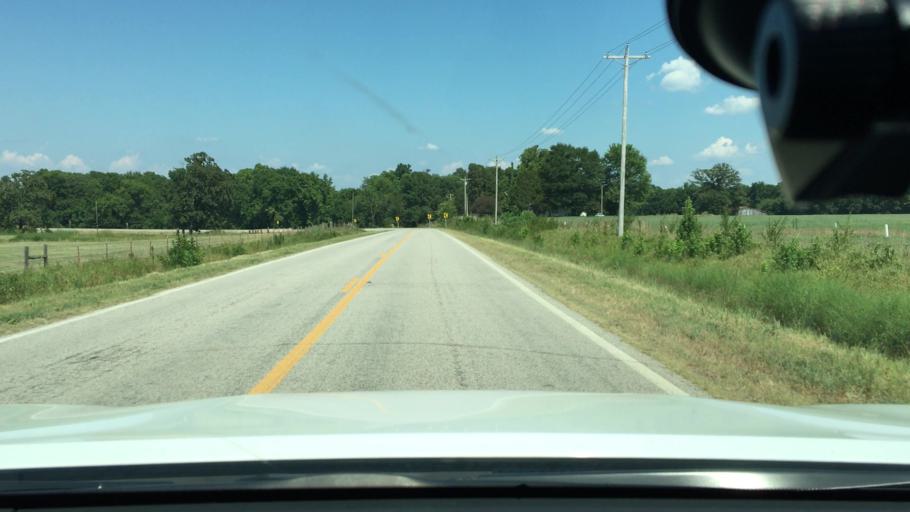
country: US
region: Arkansas
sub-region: Johnson County
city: Coal Hill
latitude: 35.3507
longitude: -93.5700
